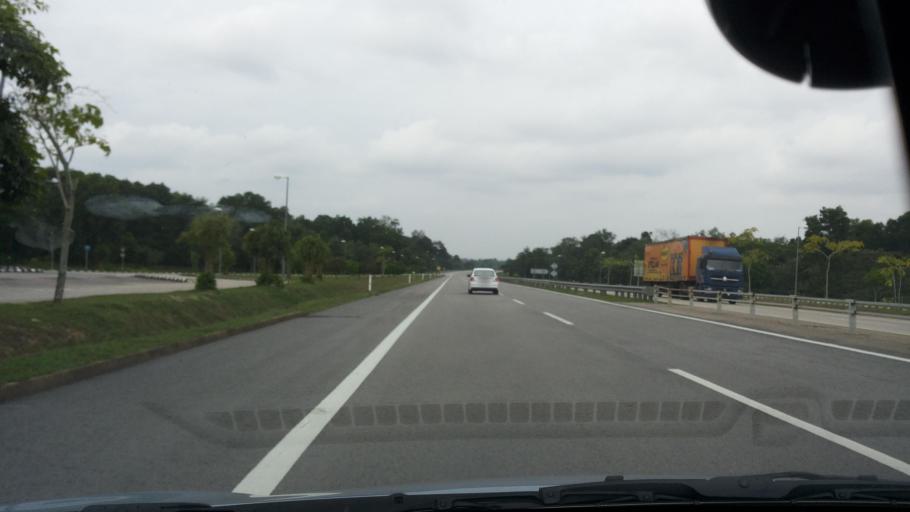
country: MY
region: Pahang
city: Kuantan
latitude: 3.8428
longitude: 103.2097
